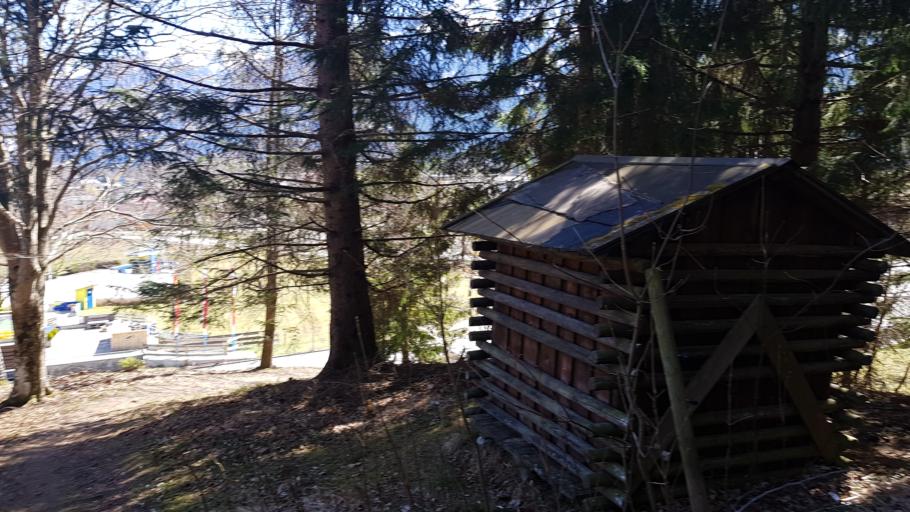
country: AT
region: Carinthia
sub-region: Politischer Bezirk Spittal an der Drau
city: Oberdrauburg
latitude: 46.6768
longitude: 12.9967
